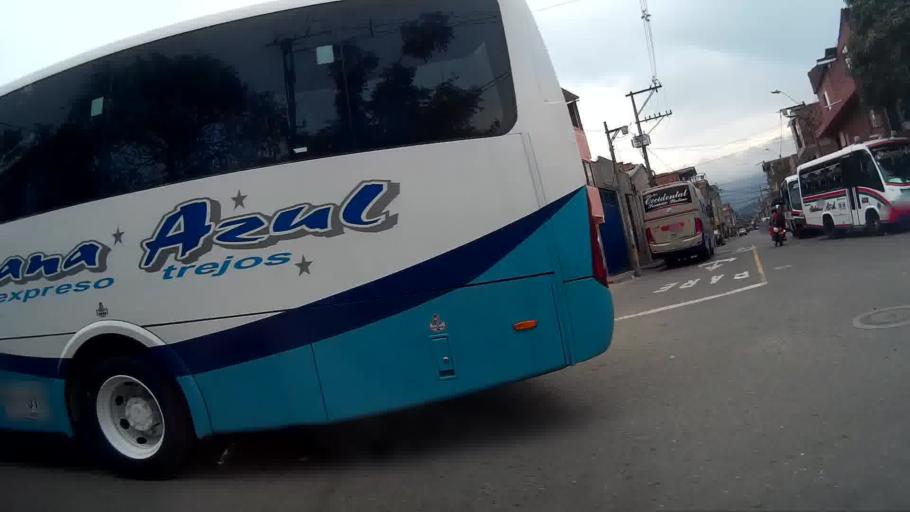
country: CO
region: Antioquia
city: Medellin
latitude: 6.2236
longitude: -75.5877
